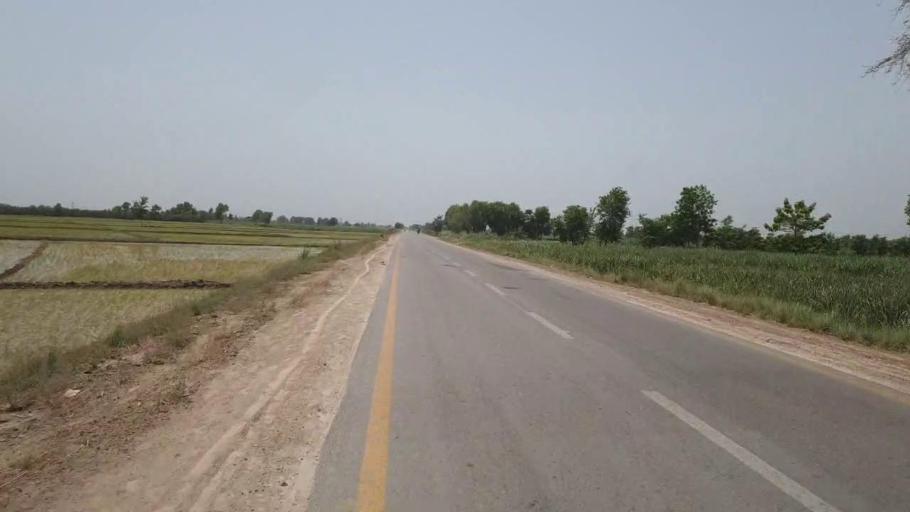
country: PK
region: Sindh
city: Moro
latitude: 26.6032
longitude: 68.0569
